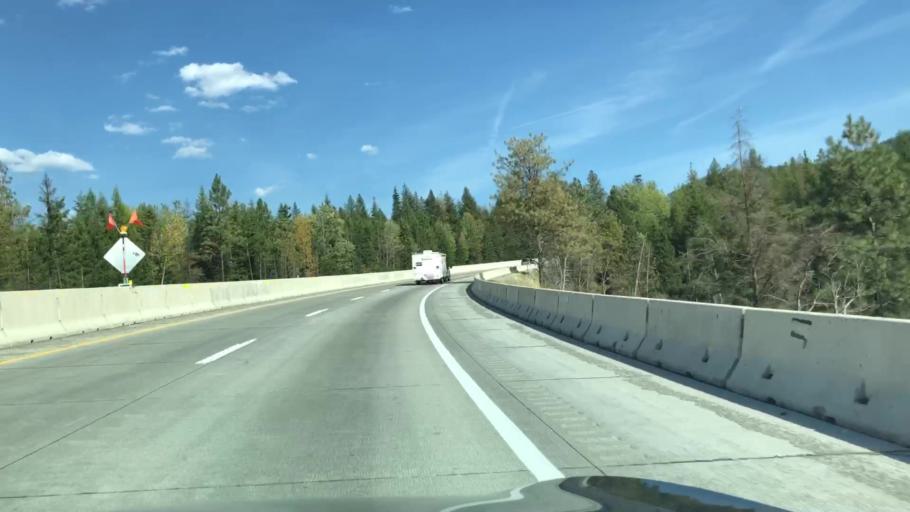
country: US
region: Idaho
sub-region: Shoshone County
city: Wallace
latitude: 47.4699
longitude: -115.7654
